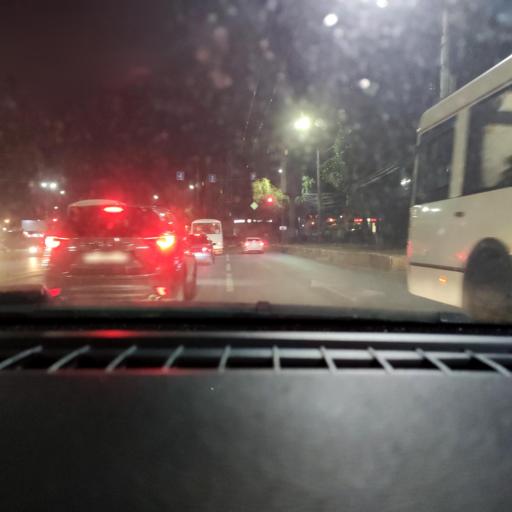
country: RU
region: Voronezj
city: Voronezh
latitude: 51.6733
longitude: 39.2534
